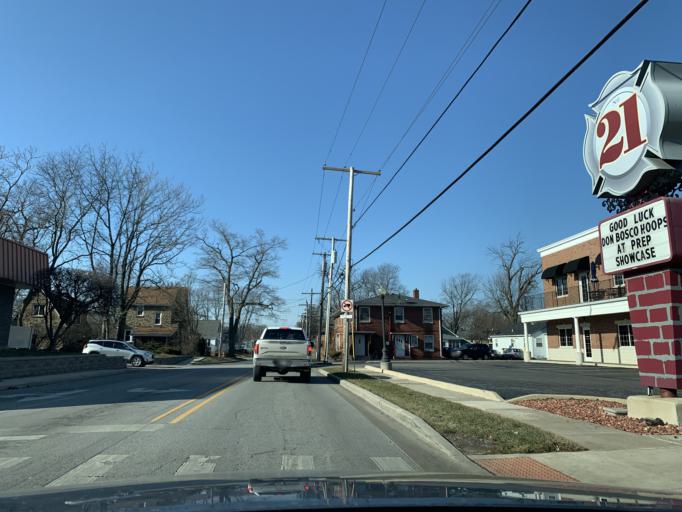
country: US
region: Indiana
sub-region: Lake County
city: Crown Point
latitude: 41.4203
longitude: -87.3644
